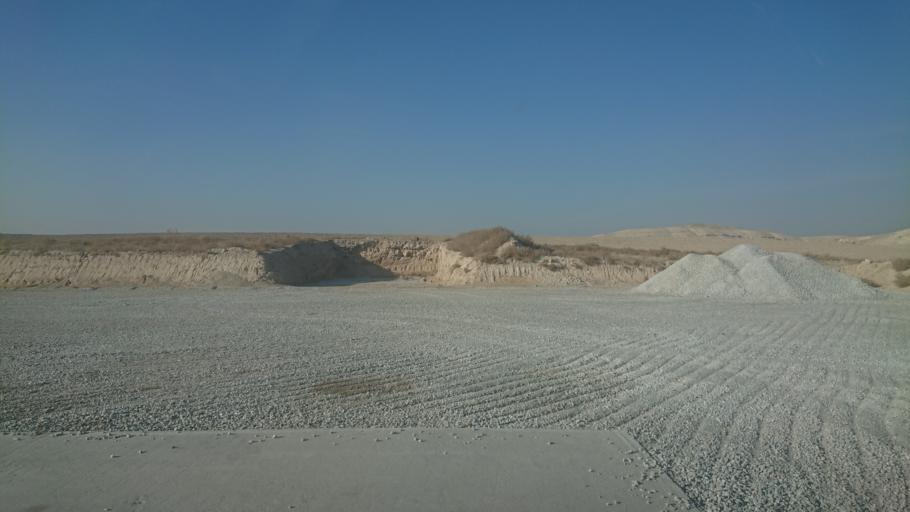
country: TR
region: Aksaray
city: Sultanhani
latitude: 38.0862
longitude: 33.6210
